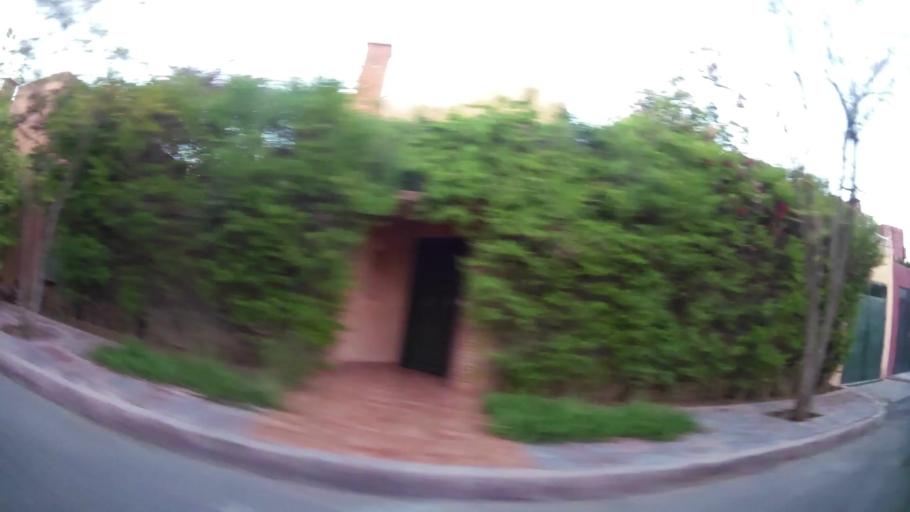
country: MA
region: Marrakech-Tensift-Al Haouz
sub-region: Marrakech
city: Marrakesh
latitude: 31.6442
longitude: -8.0227
